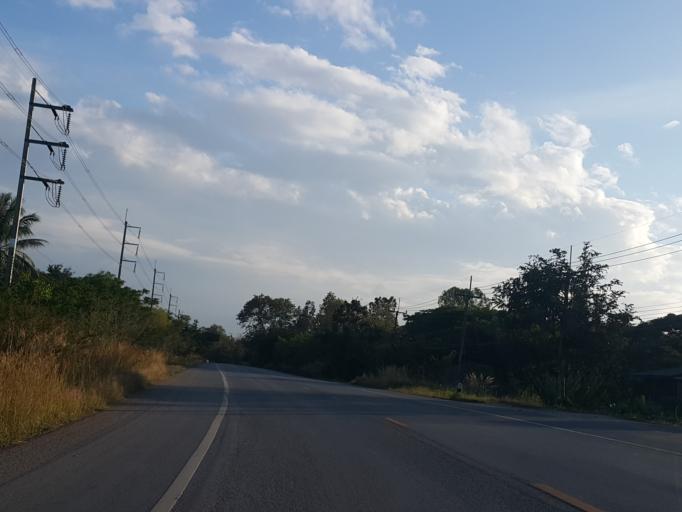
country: TH
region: Lampang
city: Lampang
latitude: 18.4457
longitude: 99.5388
